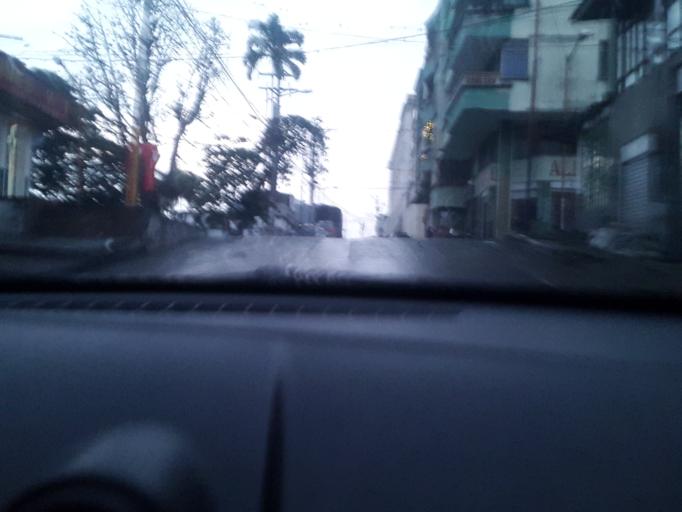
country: CO
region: Quindio
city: Armenia
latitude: 4.5379
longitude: -75.6762
